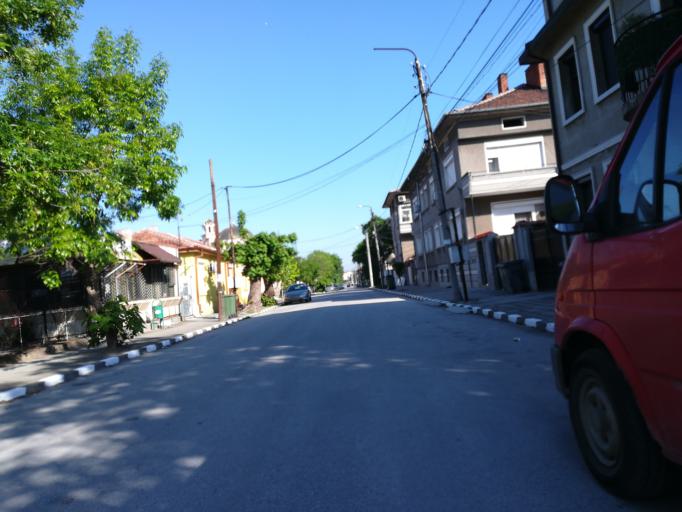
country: BG
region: Stara Zagora
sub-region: Obshtina Chirpan
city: Chirpan
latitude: 42.1014
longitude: 25.2245
